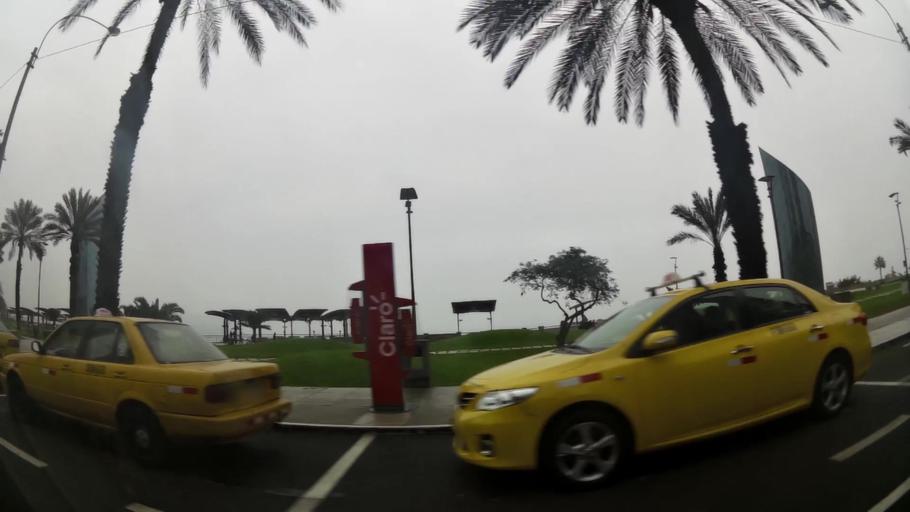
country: PE
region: Lima
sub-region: Lima
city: San Isidro
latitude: -12.1313
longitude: -77.0303
